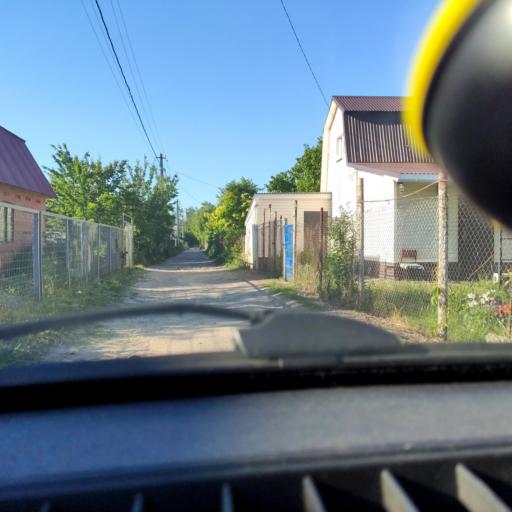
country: RU
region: Samara
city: Tol'yatti
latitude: 53.5959
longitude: 49.3150
